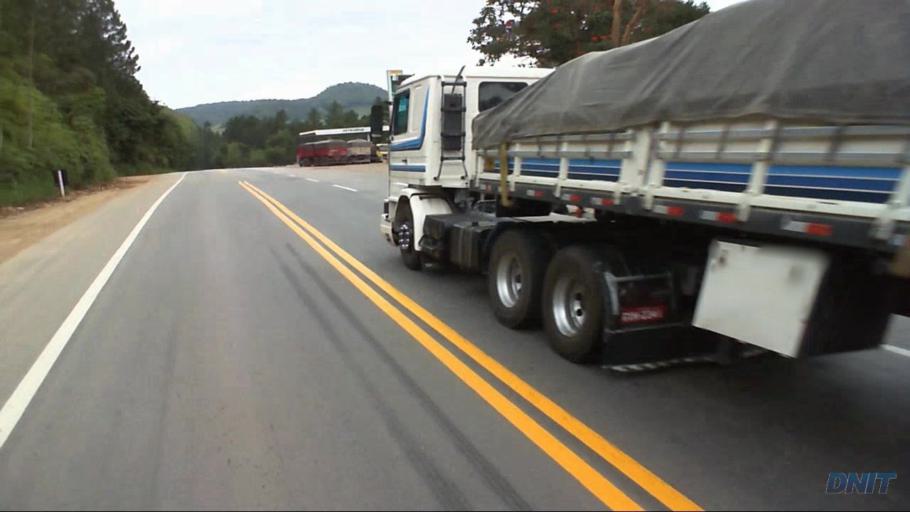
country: BR
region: Minas Gerais
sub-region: Nova Era
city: Nova Era
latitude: -19.7295
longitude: -43.0150
